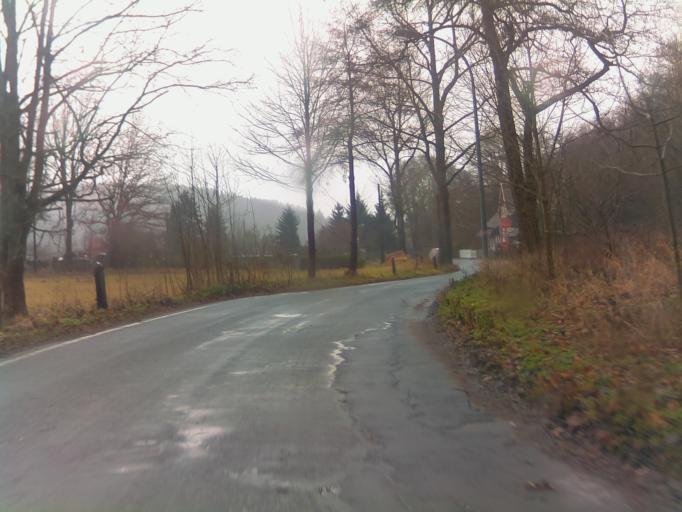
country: DE
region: Thuringia
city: Grafenroda
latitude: 50.7316
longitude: 10.7918
